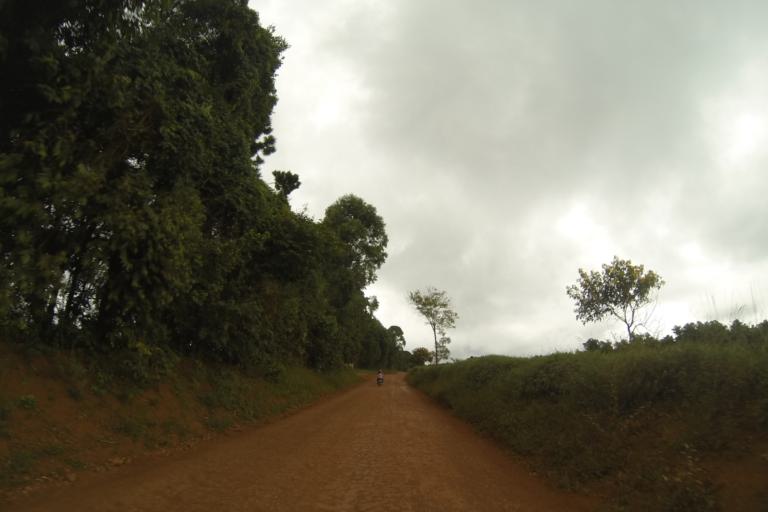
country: BR
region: Minas Gerais
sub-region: Campos Altos
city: Campos Altos
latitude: -19.8004
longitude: -46.3558
